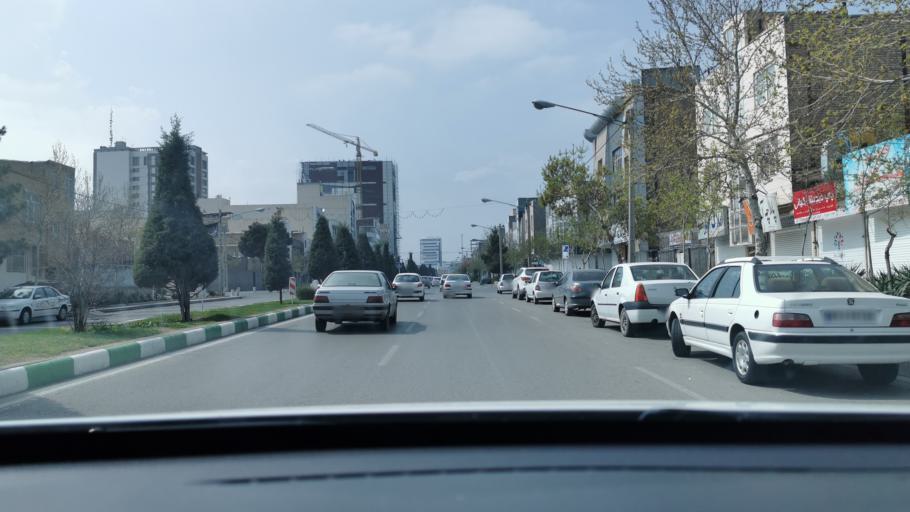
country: IR
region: Razavi Khorasan
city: Mashhad
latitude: 36.3281
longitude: 59.5329
